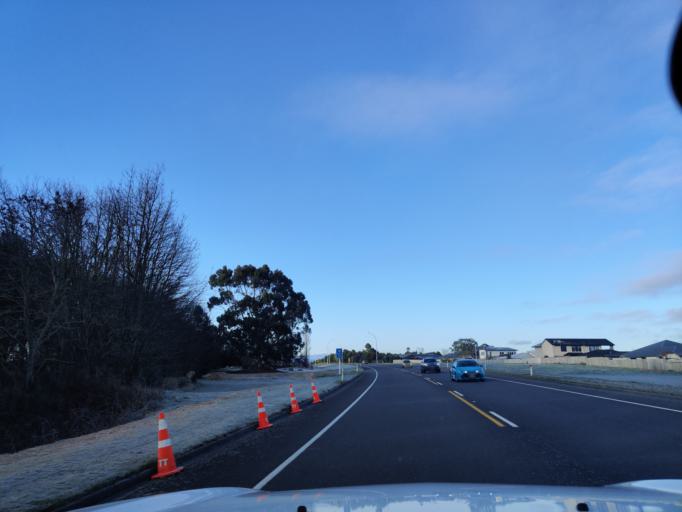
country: NZ
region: Waikato
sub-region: Taupo District
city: Taupo
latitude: -38.7343
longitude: 176.0720
